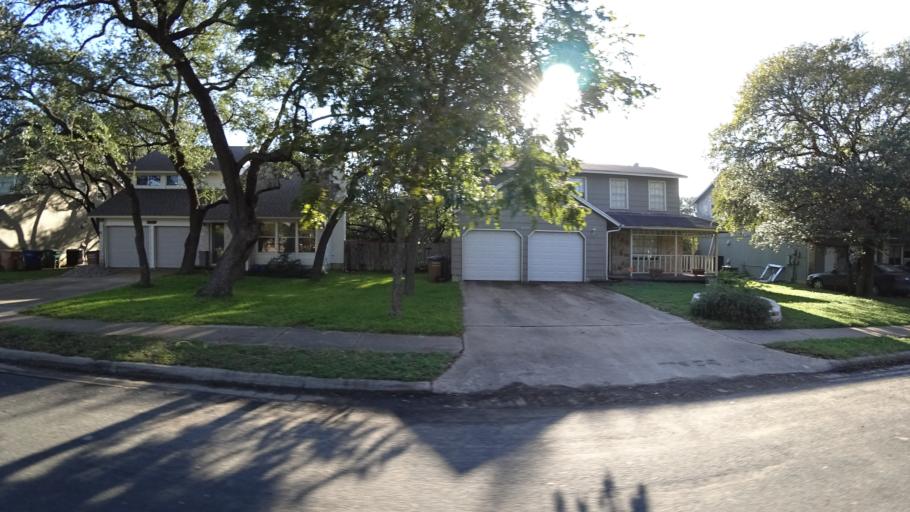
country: US
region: Texas
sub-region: Travis County
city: Shady Hollow
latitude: 30.2073
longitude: -97.8462
